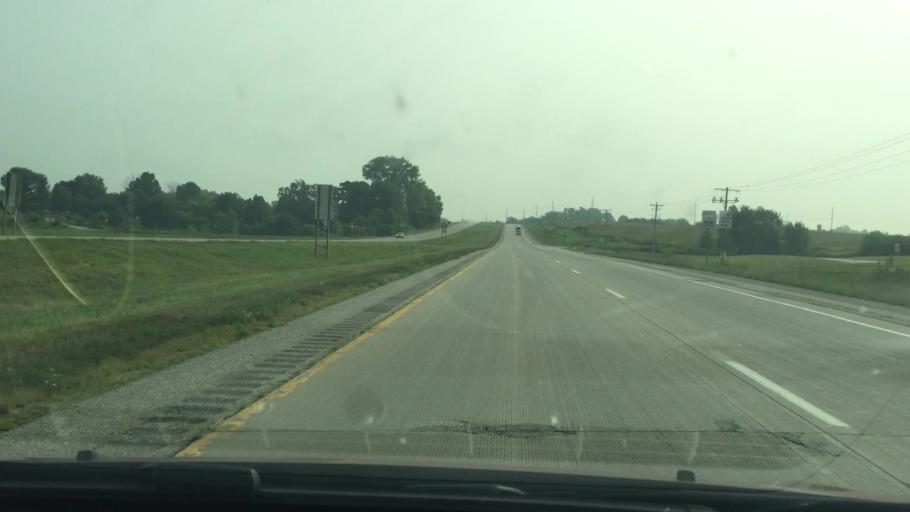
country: US
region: Iowa
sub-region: Muscatine County
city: Muscatine
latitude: 41.4604
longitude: -91.0154
